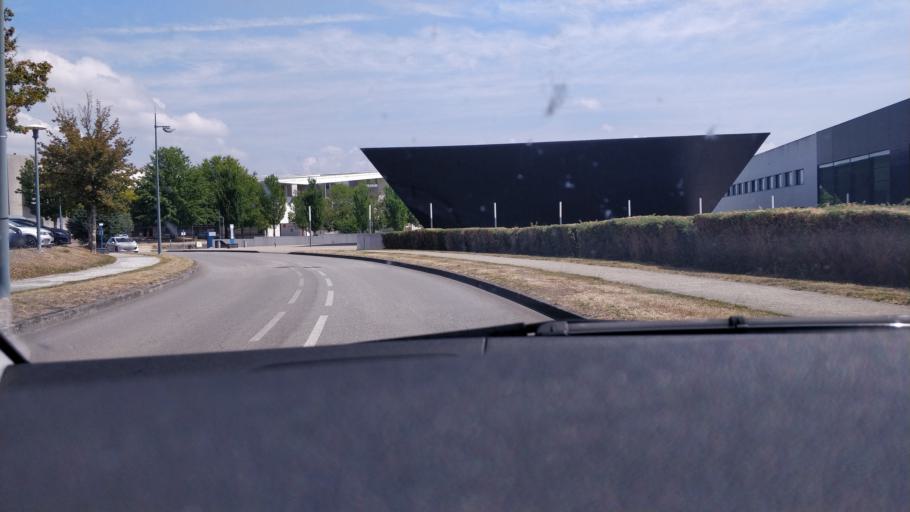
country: FR
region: Limousin
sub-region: Departement de la Haute-Vienne
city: Le Palais-sur-Vienne
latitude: 45.8601
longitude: 1.2932
